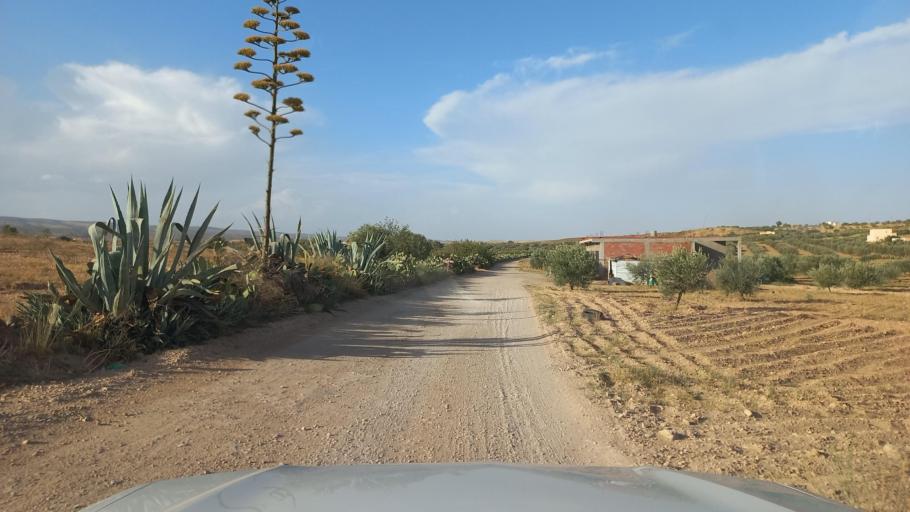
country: TN
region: Al Qasrayn
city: Kasserine
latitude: 35.2424
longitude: 8.9169
